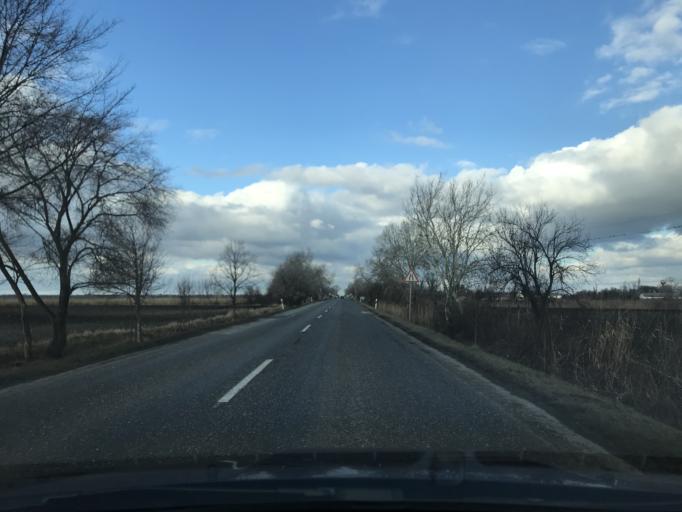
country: HU
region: Bacs-Kiskun
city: Sukosd
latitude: 46.3327
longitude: 18.9816
